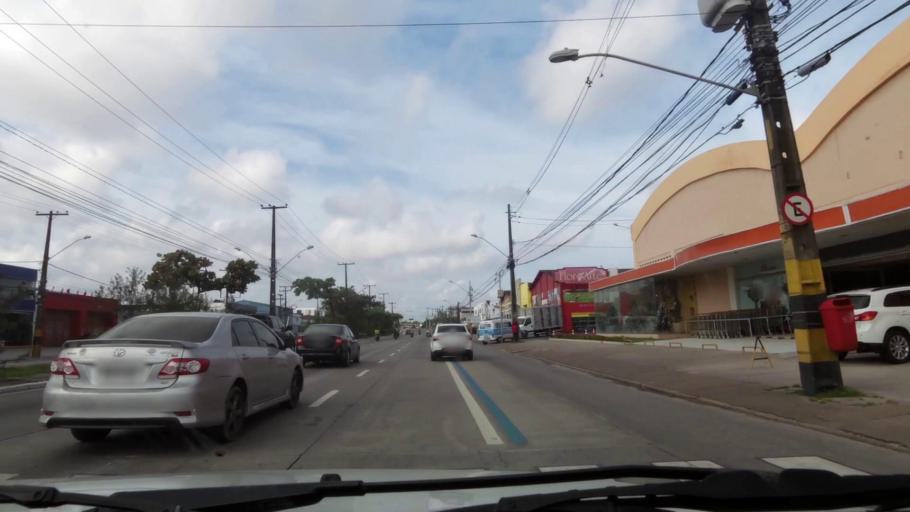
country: BR
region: Pernambuco
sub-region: Recife
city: Recife
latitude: -8.0837
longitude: -34.9067
